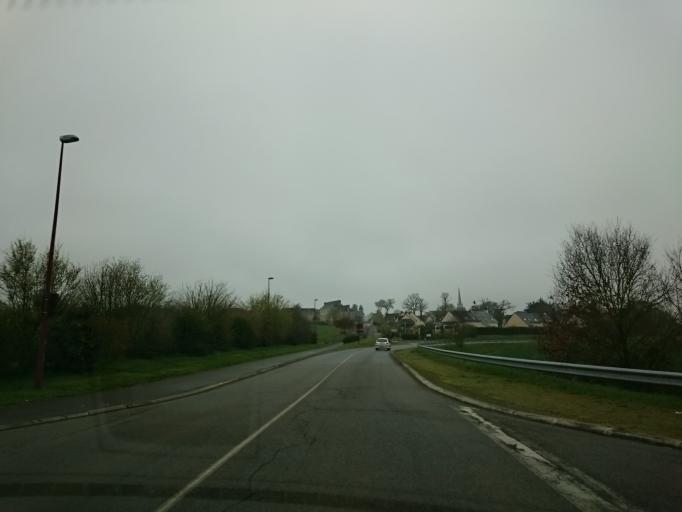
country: FR
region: Brittany
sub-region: Departement d'Ille-et-Vilaine
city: Bourg-des-Comptes
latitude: 47.9320
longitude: -1.7328
